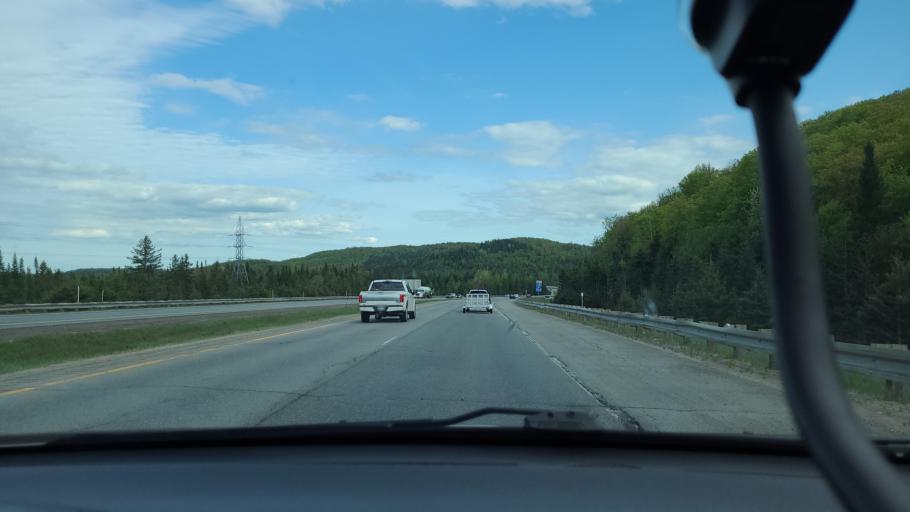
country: CA
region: Quebec
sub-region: Laurentides
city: Sainte-Agathe-des-Monts
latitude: 46.0330
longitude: -74.2671
